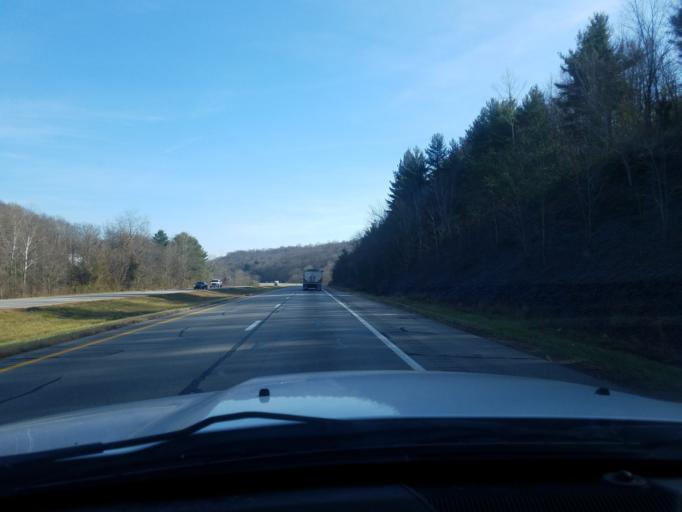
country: US
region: Ohio
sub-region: Pike County
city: Piketon
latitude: 39.0605
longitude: -83.1032
